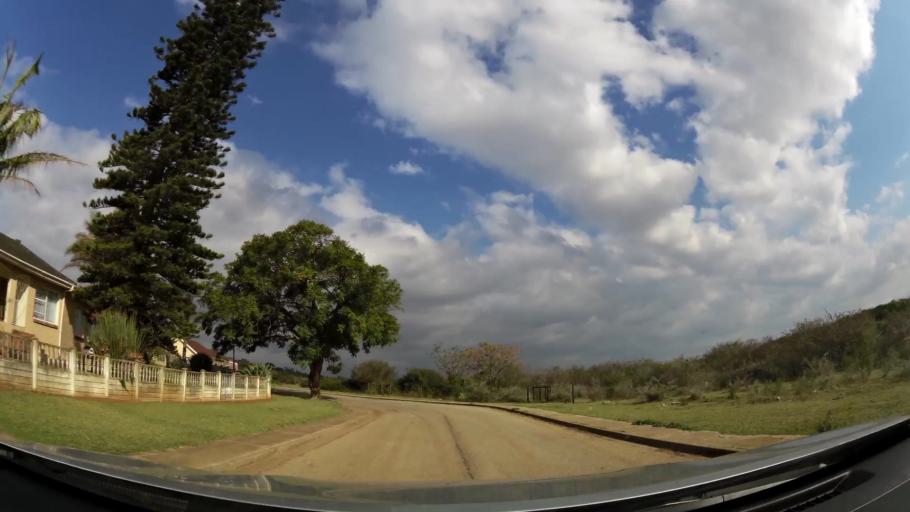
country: ZA
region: Eastern Cape
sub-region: Nelson Mandela Bay Metropolitan Municipality
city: Uitenhage
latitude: -33.7312
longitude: 25.4050
